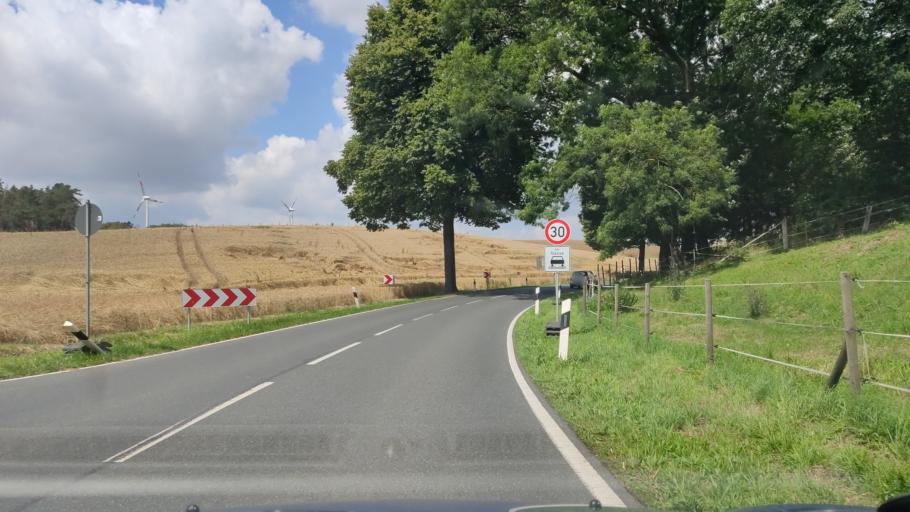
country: DE
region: Lower Saxony
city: Halle
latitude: 51.9992
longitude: 9.5521
